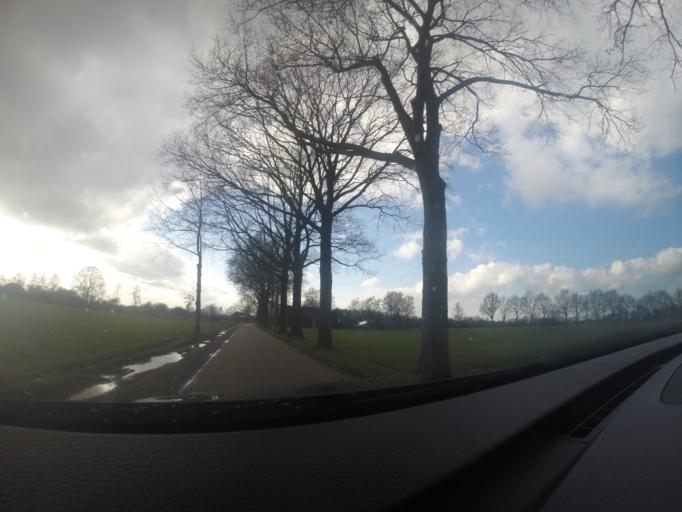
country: NL
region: Gelderland
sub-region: Oude IJsselstreek
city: Varsseveld
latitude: 51.9946
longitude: 6.4409
